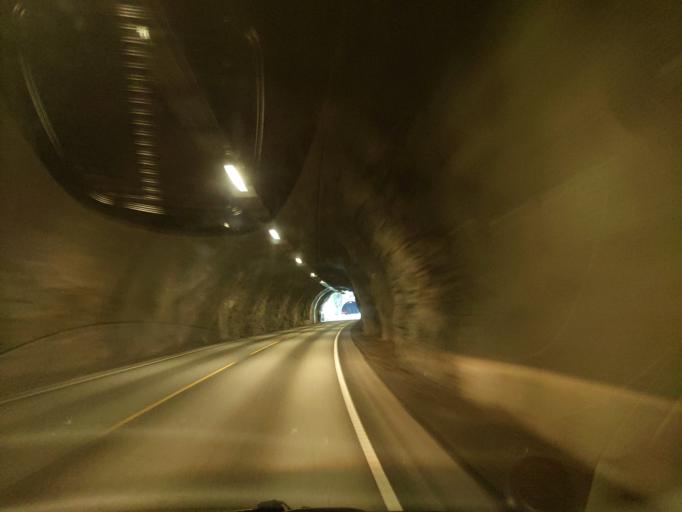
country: NO
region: Hordaland
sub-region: Osteroy
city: Lonevag
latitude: 60.6986
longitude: 5.5771
